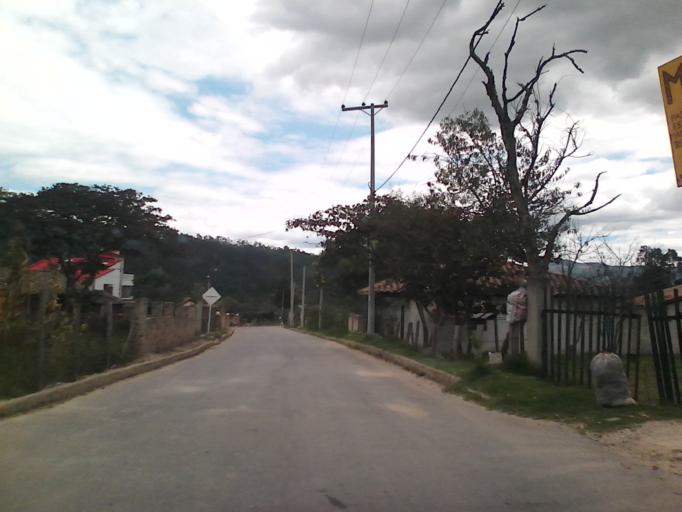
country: CO
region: Boyaca
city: Duitama
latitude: 5.8225
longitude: -73.0728
